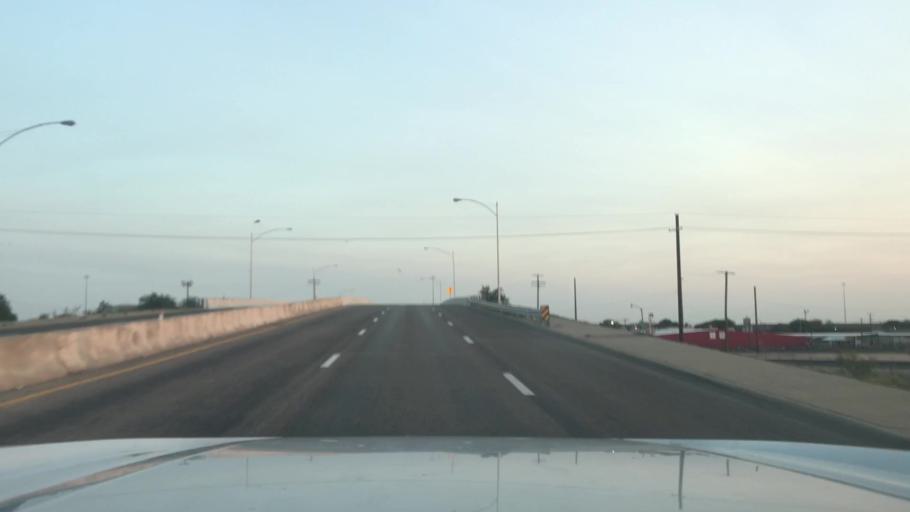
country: US
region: Texas
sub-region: Lubbock County
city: Lubbock
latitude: 33.5988
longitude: -101.8545
